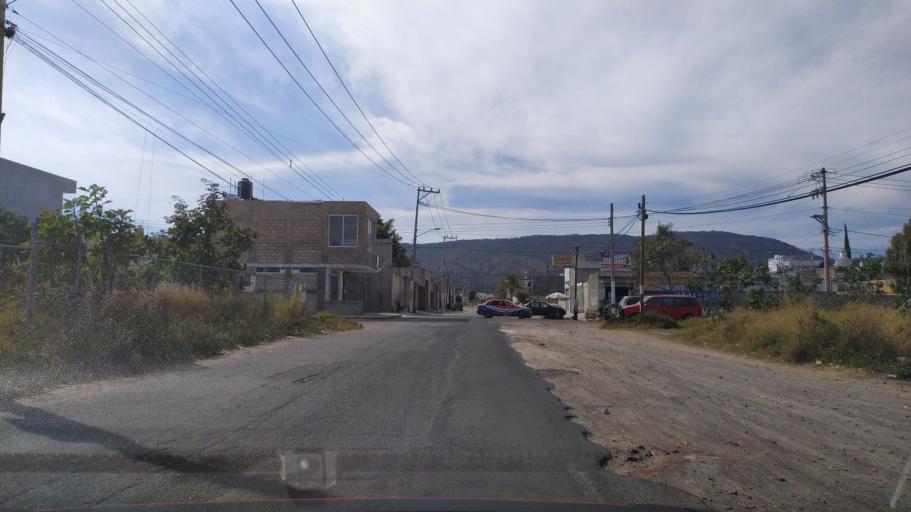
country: MX
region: Jalisco
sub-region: Tlajomulco de Zuniga
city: Palomar
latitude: 20.6284
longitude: -103.4723
